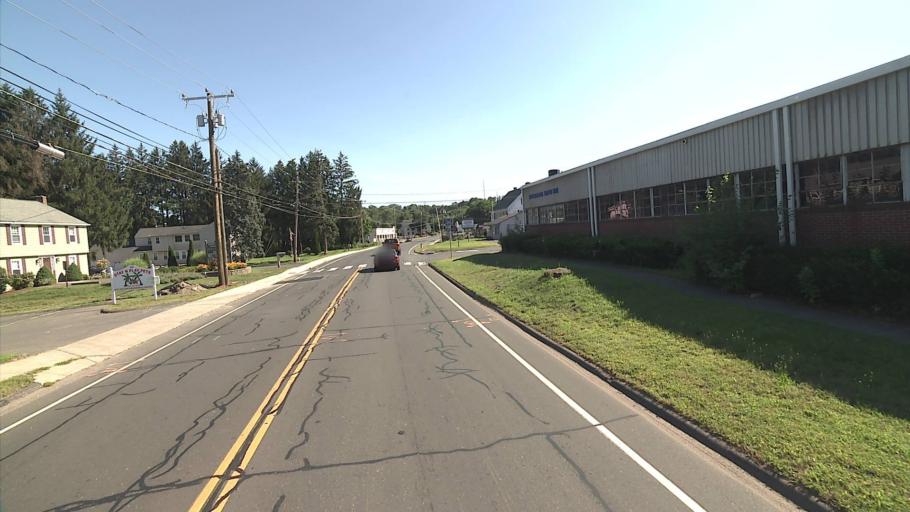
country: US
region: Connecticut
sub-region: Hartford County
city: Plainville
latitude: 41.6115
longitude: -72.8759
